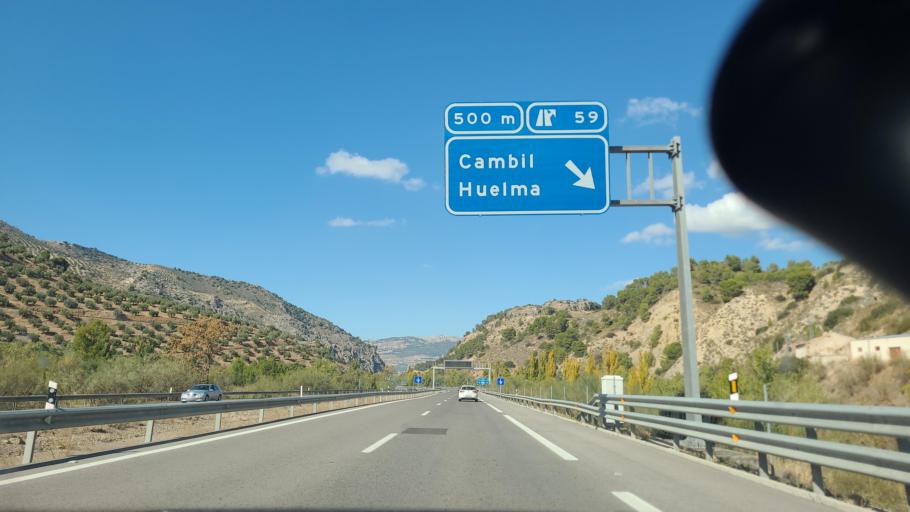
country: ES
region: Andalusia
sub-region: Provincia de Jaen
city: Cambil
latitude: 37.6680
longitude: -3.6192
